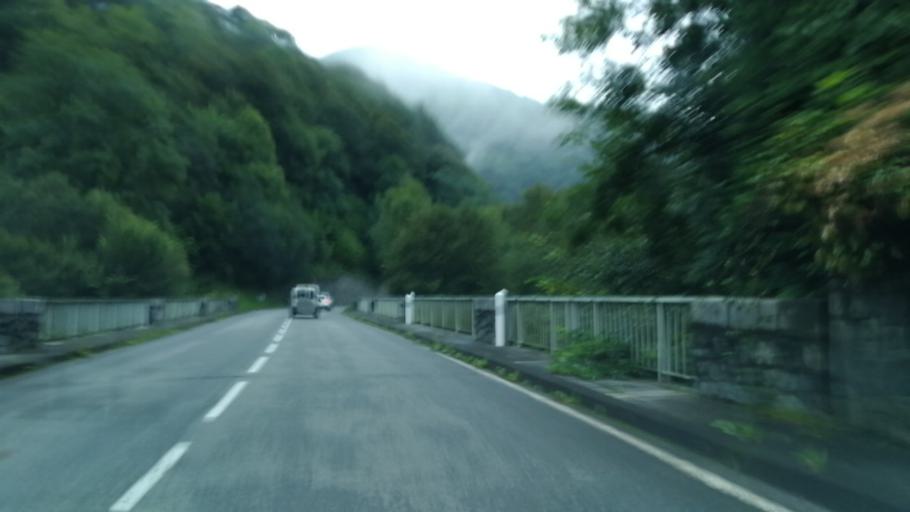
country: FR
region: Aquitaine
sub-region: Departement des Pyrenees-Atlantiques
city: Arette
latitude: 43.0447
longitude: -0.6006
